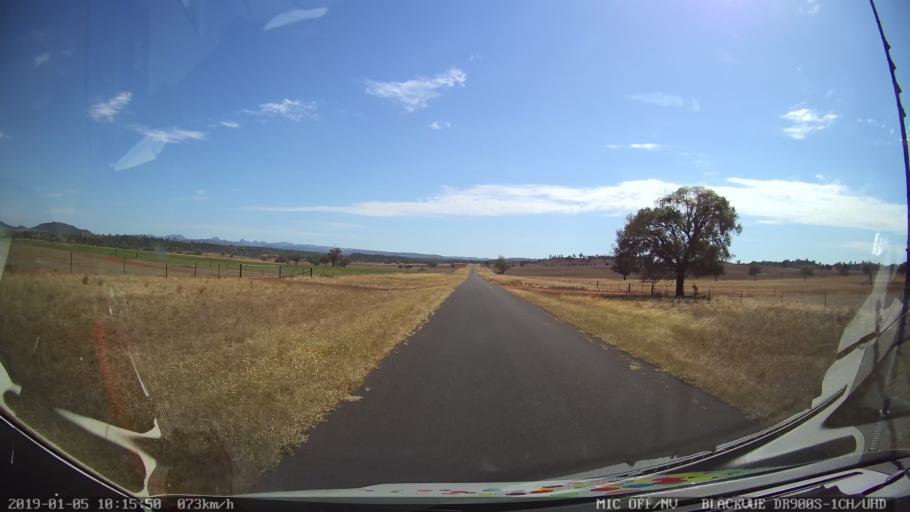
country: AU
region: New South Wales
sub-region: Gilgandra
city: Gilgandra
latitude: -31.5806
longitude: 148.9467
